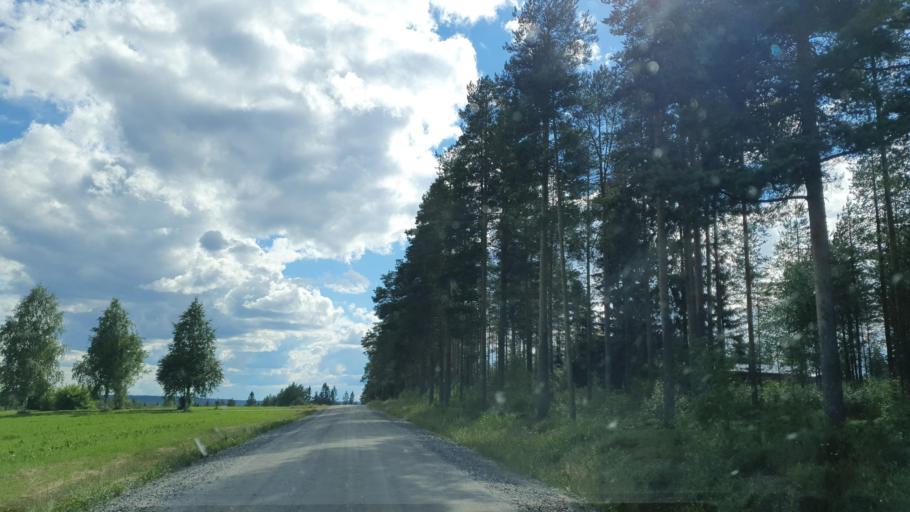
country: FI
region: Kainuu
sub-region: Kehys-Kainuu
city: Kuhmo
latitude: 64.1282
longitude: 29.6448
